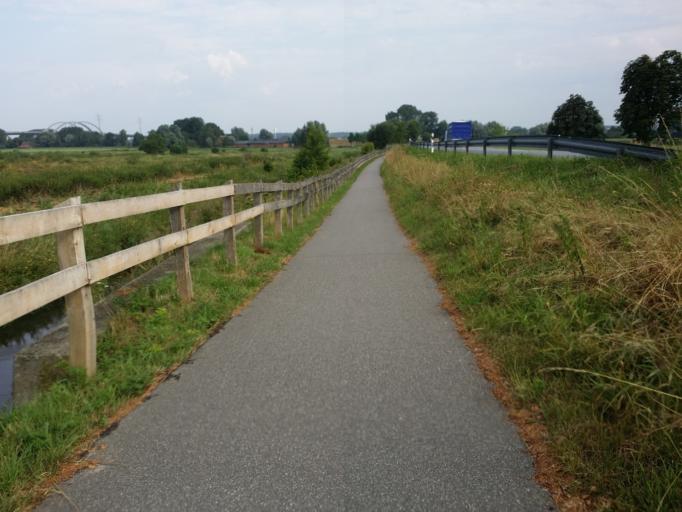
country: DE
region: Schleswig-Holstein
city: Heiligenstedten
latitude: 53.9167
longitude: 9.4885
